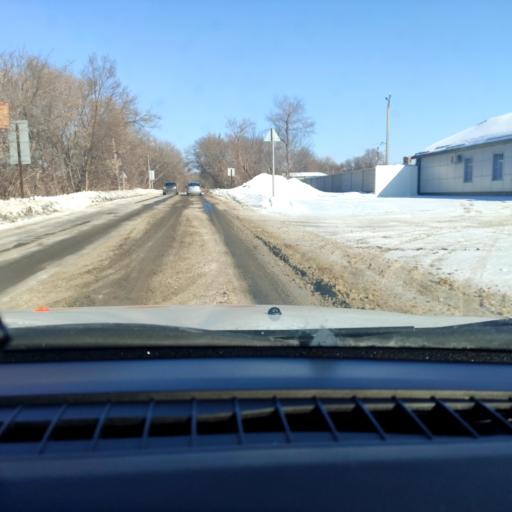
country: RU
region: Samara
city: Novokuybyshevsk
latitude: 53.1198
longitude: 49.9151
